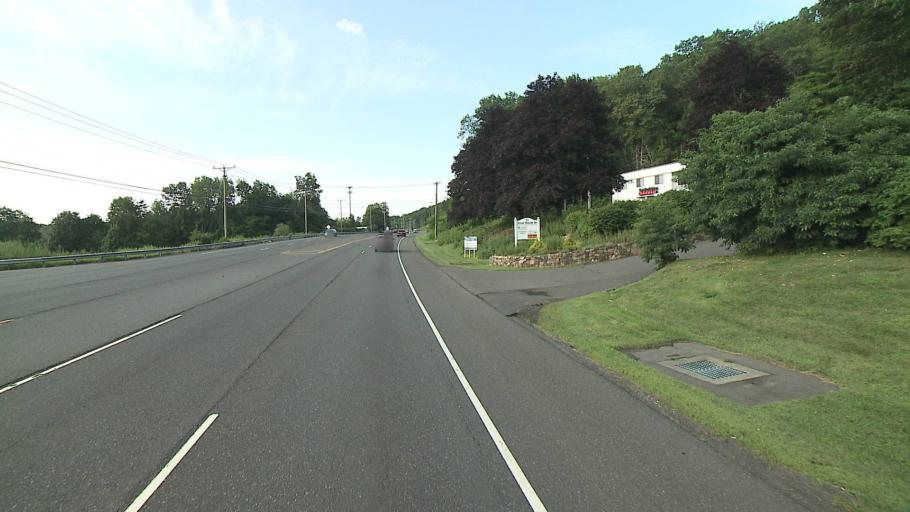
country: US
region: Connecticut
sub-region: Fairfield County
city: Danbury
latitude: 41.3388
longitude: -73.4700
